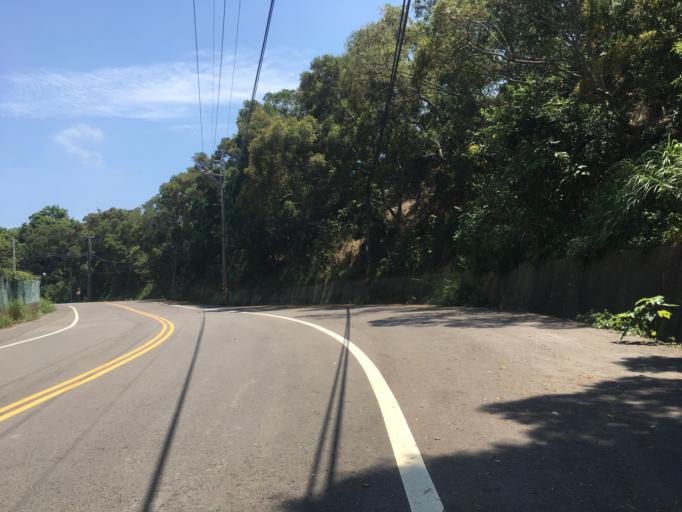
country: TW
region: Taiwan
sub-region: Hsinchu
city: Hsinchu
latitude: 24.7383
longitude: 120.9855
